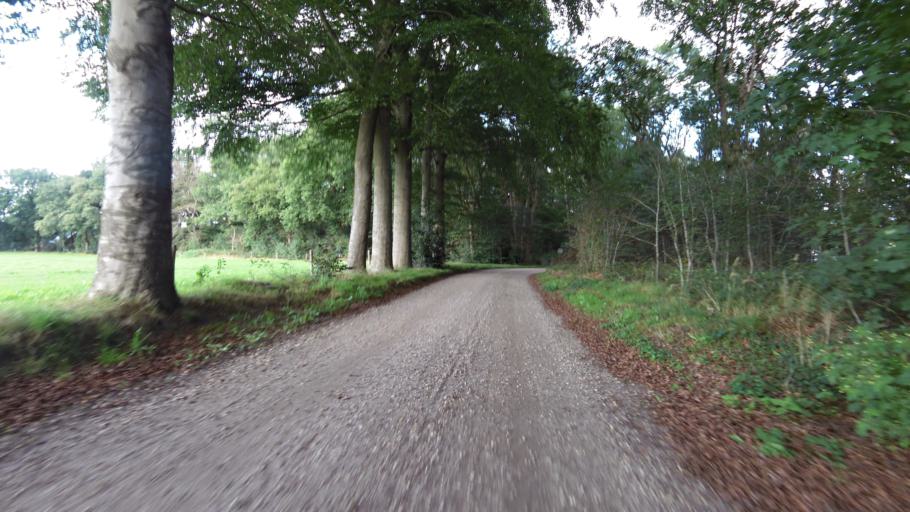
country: NL
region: Gelderland
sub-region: Gemeente Apeldoorn
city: Uddel
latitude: 52.2531
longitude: 5.7842
